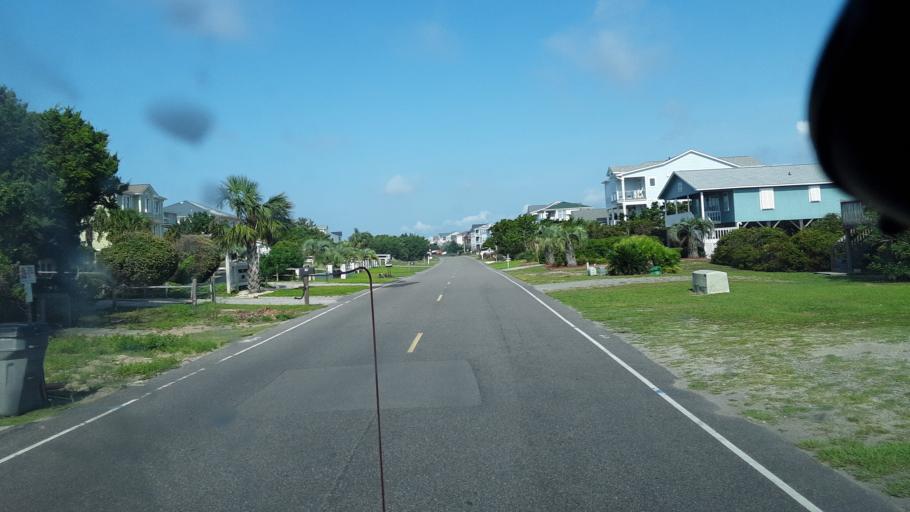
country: US
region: North Carolina
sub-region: Brunswick County
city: Southport
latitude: 33.8954
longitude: -78.0460
